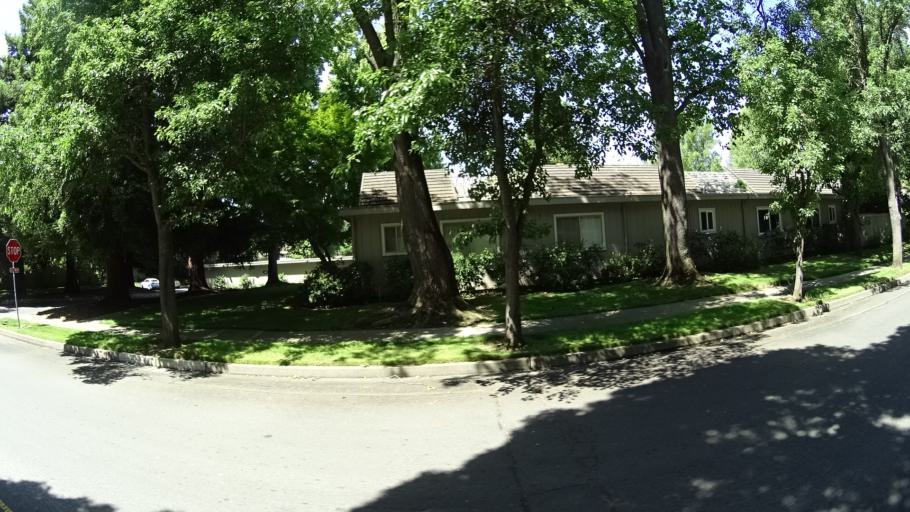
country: US
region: California
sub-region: Sacramento County
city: Arden-Arcade
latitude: 38.5692
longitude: -121.4110
